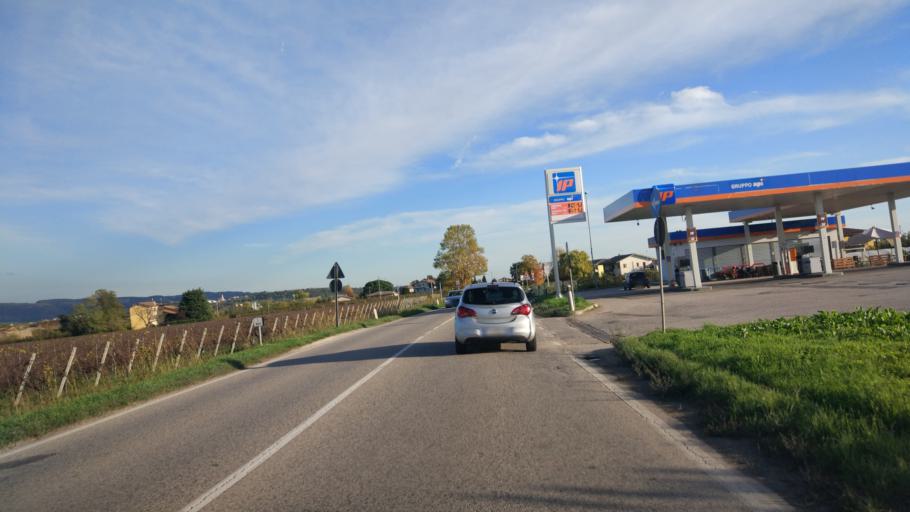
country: IT
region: Veneto
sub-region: Provincia di Verona
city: Ospedaletto
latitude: 45.5035
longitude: 10.8513
